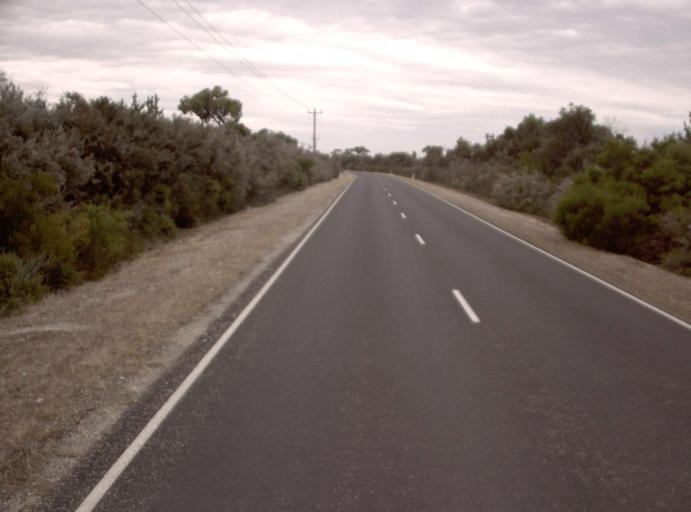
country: AU
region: Victoria
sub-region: Wellington
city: Sale
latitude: -38.1903
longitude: 147.3679
